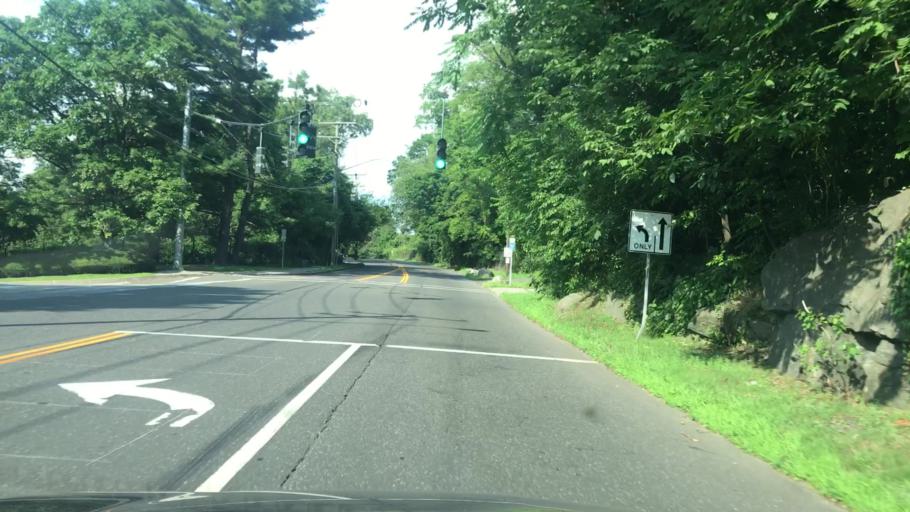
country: US
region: Connecticut
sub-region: Fairfield County
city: Byram
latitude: 41.0107
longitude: -73.6449
